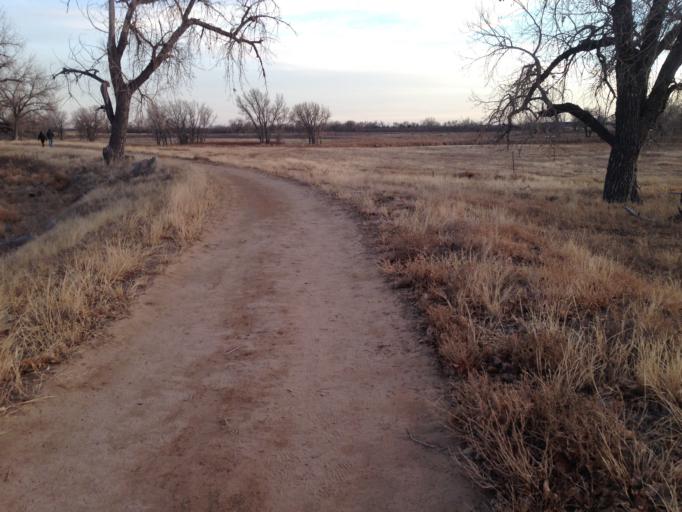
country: US
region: Colorado
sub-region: Adams County
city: Derby
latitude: 39.8157
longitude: -104.8548
